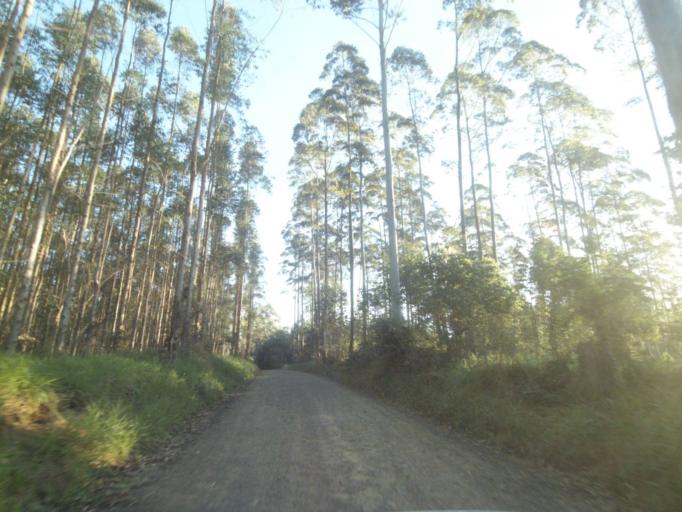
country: BR
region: Parana
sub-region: Telemaco Borba
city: Telemaco Borba
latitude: -24.4933
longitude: -50.5981
